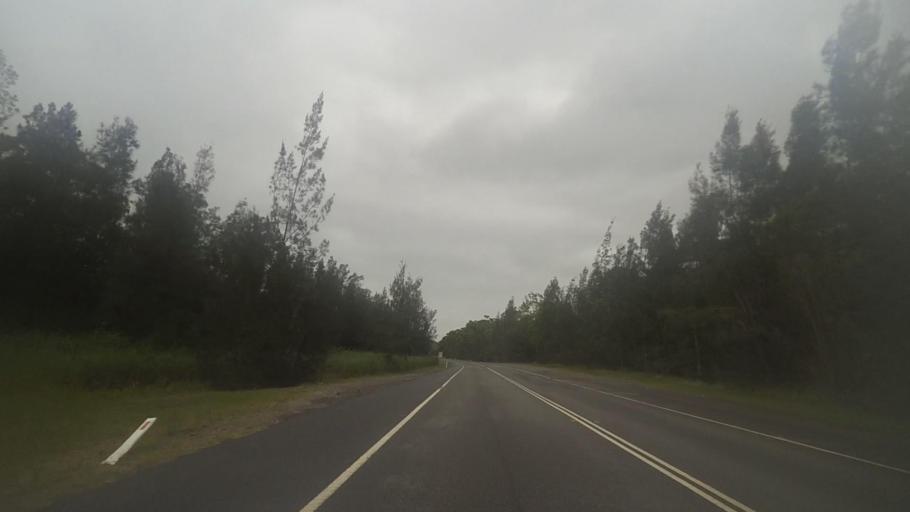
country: AU
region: New South Wales
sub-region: Port Stephens Shire
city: Port Stephens
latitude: -32.6339
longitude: 151.9956
